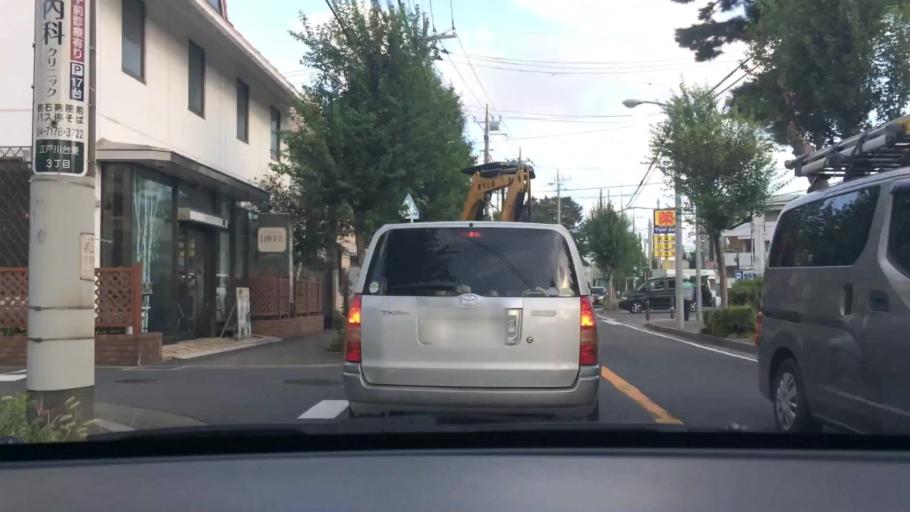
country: JP
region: Chiba
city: Nagareyama
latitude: 35.8995
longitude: 139.9119
